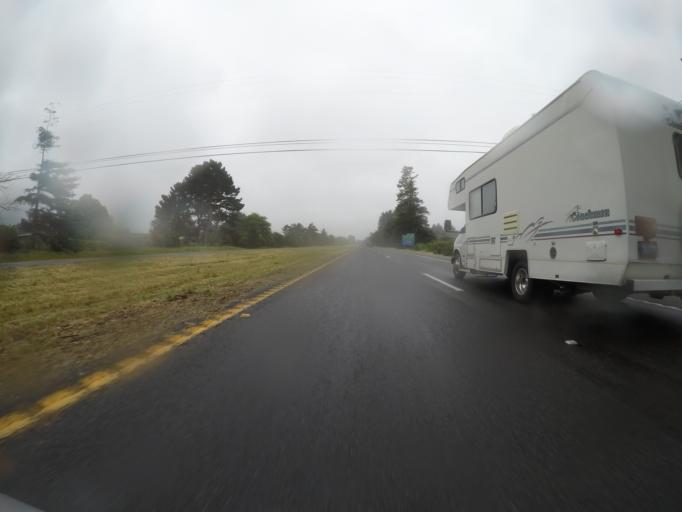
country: US
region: California
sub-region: Humboldt County
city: McKinleyville
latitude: 40.9510
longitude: -124.1163
